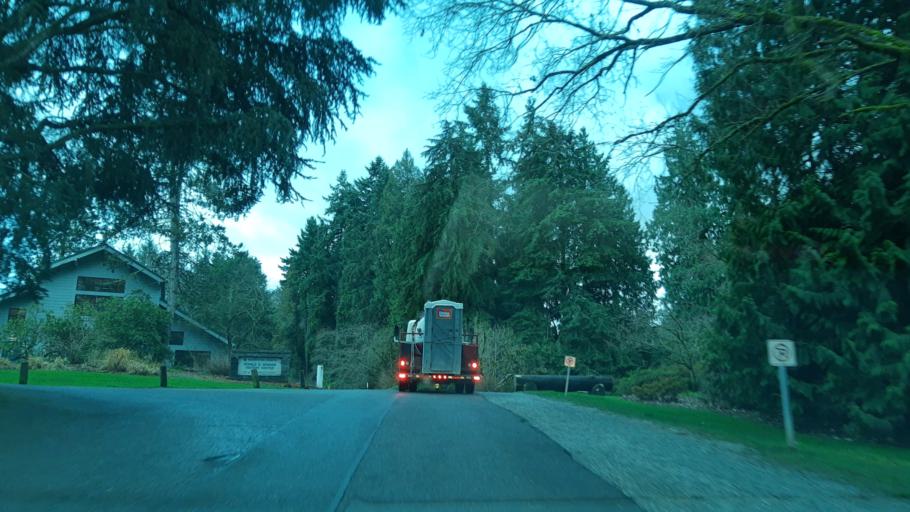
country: US
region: Washington
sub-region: King County
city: Seattle
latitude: 47.6404
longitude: -122.2946
